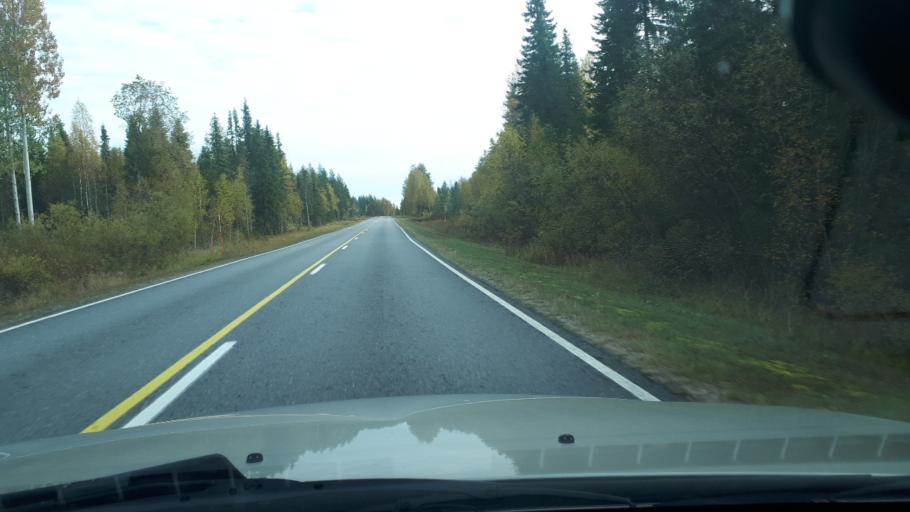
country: FI
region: Lapland
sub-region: Rovaniemi
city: Ranua
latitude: 65.9623
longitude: 25.9535
